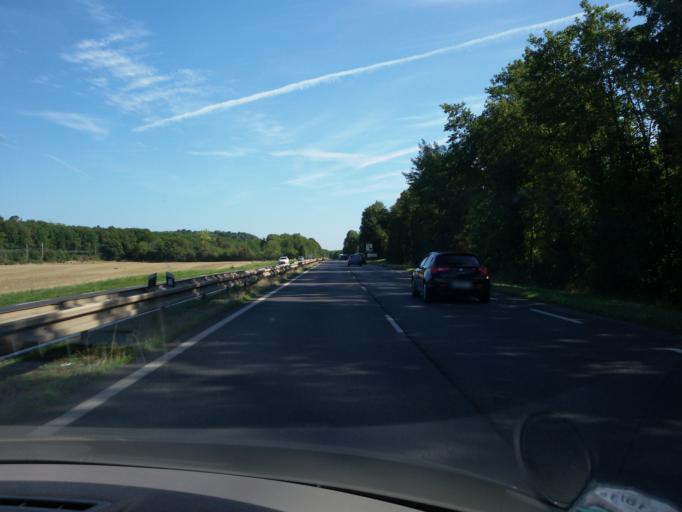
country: FR
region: Ile-de-France
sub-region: Departement de l'Essonne
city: Morigny-Champigny
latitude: 48.4671
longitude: 2.1830
